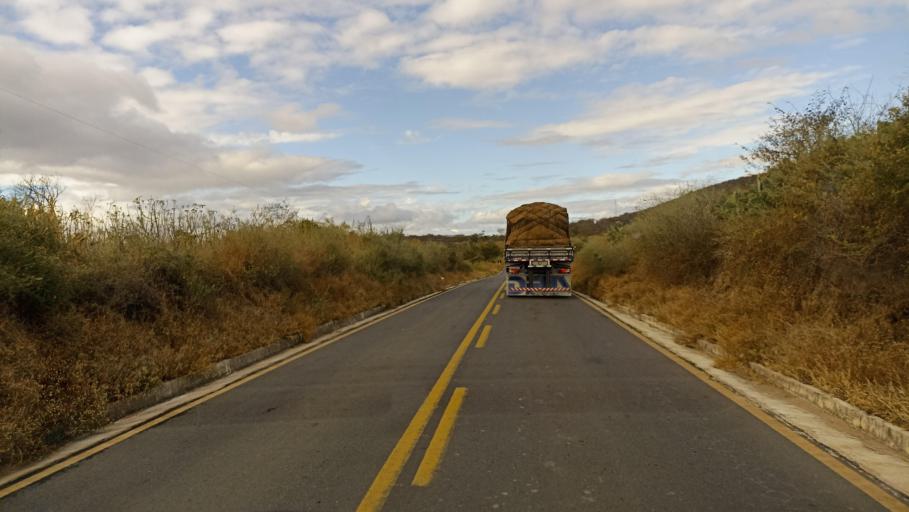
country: BR
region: Minas Gerais
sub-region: Itinga
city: Itinga
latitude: -16.5944
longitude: -41.6956
